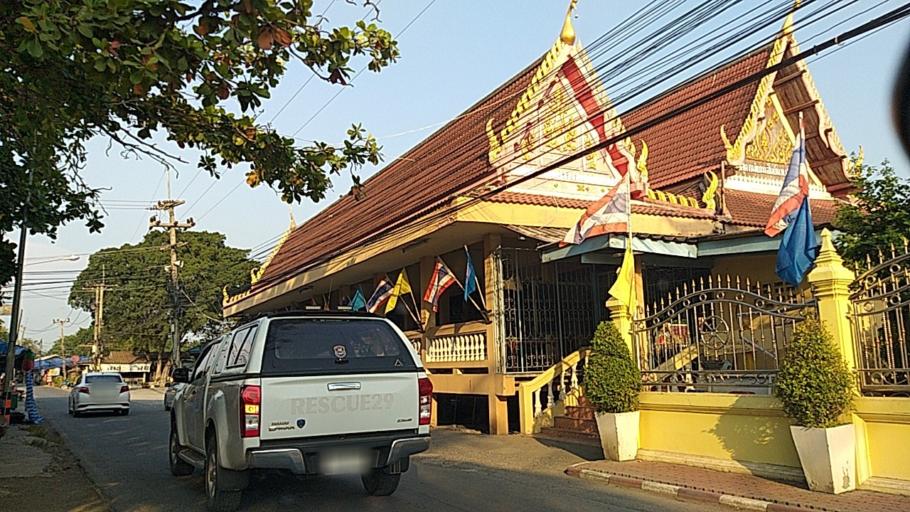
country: TH
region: Sara Buri
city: Nong Khae
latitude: 14.2755
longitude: 100.8221
